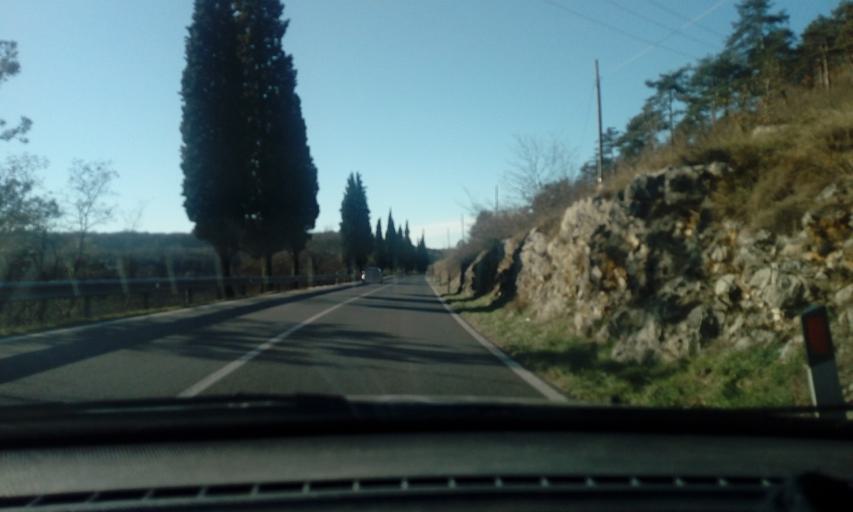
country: IT
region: Friuli Venezia Giulia
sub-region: Provincia di Gorizia
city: Savogna d'Isonzo
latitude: 45.8722
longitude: 13.5788
